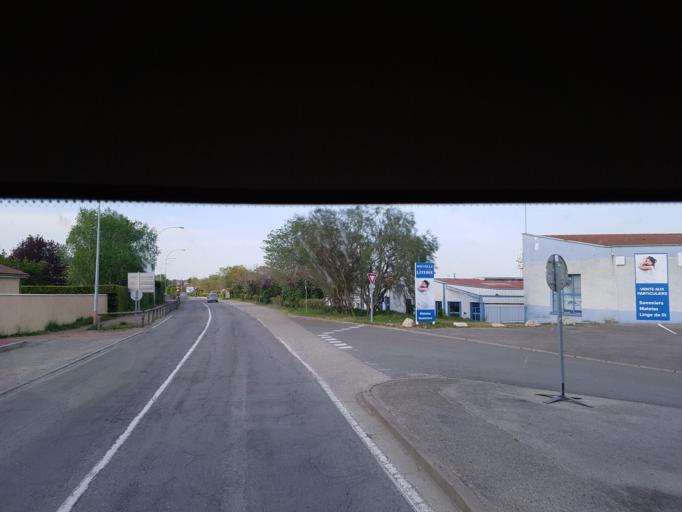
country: FR
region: Rhone-Alpes
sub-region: Departement du Rhone
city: Brindas
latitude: 45.7187
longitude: 4.6969
